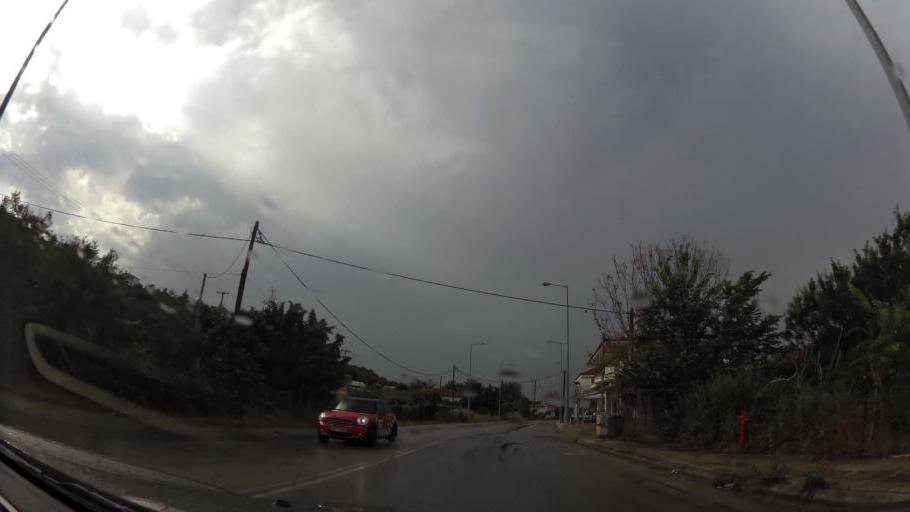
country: GR
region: Central Macedonia
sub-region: Nomos Imathias
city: Veroia
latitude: 40.5394
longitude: 22.1969
